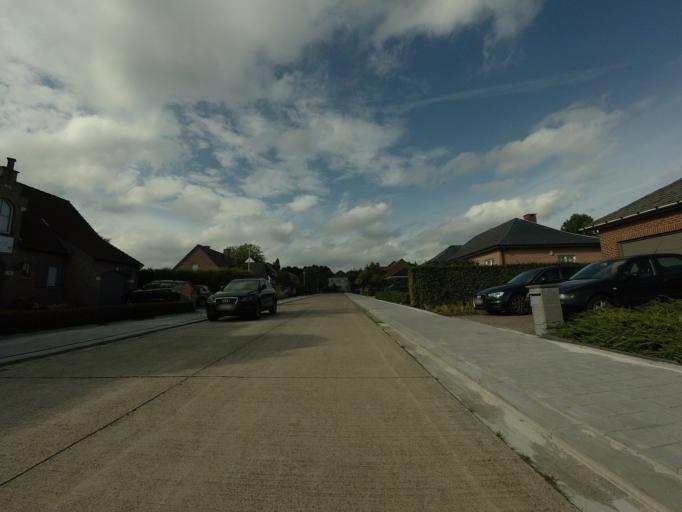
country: BE
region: Flanders
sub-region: Provincie Antwerpen
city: Rumst
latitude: 51.1029
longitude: 4.4005
